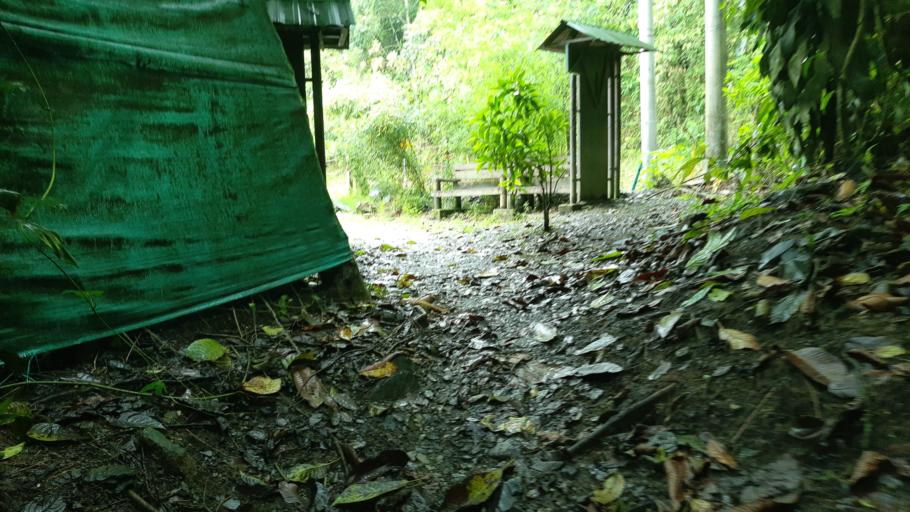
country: CO
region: Boyaca
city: Santa Maria
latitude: 4.9188
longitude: -73.3042
